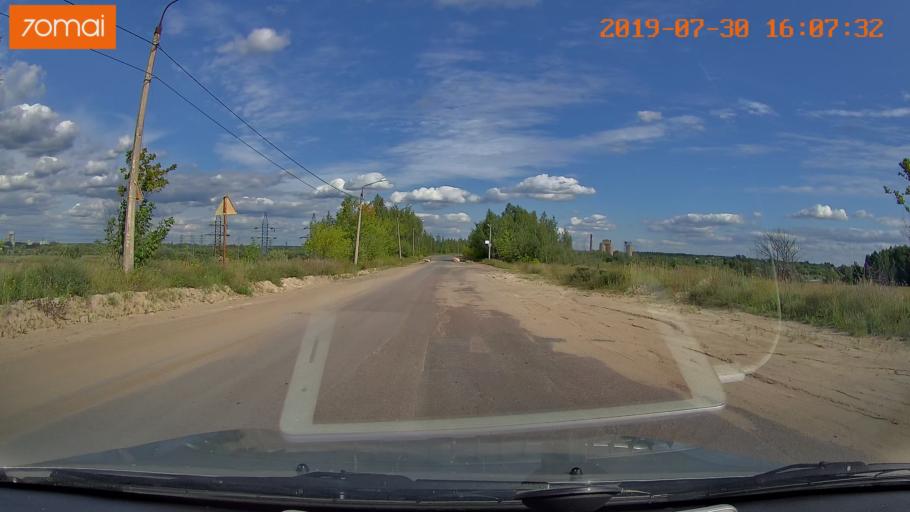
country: RU
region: Moskovskaya
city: Peski
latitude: 55.2489
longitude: 38.7203
